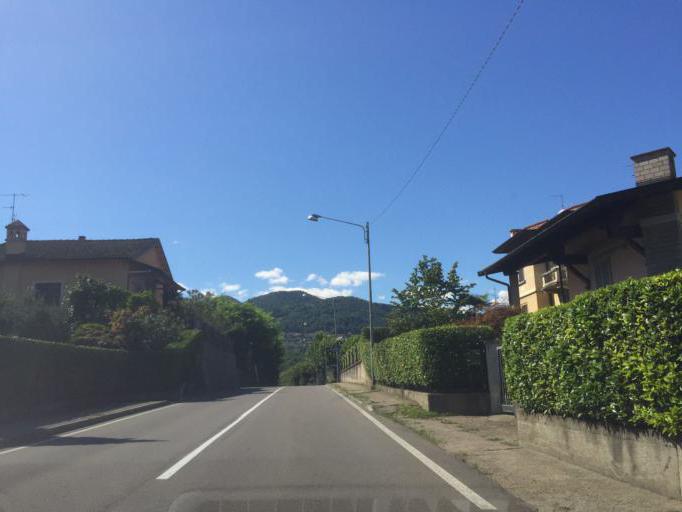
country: IT
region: Lombardy
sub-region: Provincia di Varese
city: Lavena Ponte Tresa
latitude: 45.9575
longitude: 8.8698
